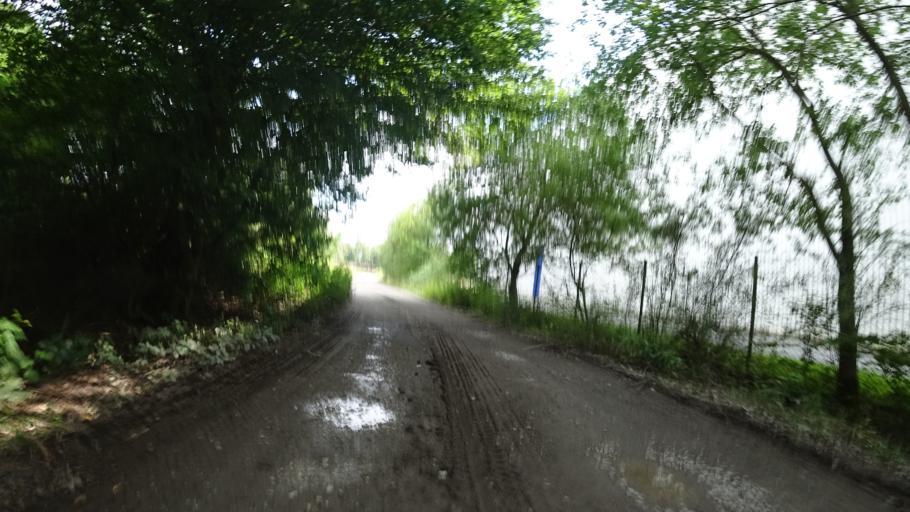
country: DE
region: North Rhine-Westphalia
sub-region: Regierungsbezirk Detmold
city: Guetersloh
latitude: 51.9270
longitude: 8.4131
